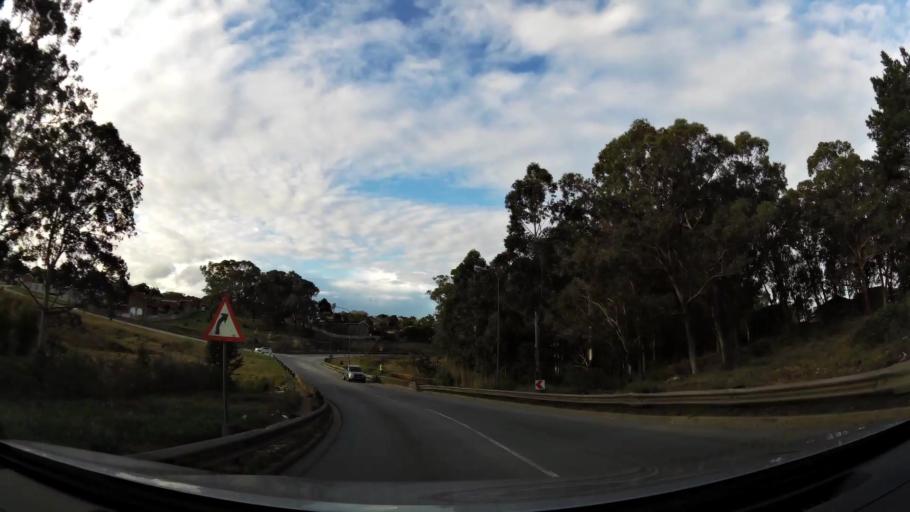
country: ZA
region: Eastern Cape
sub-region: Nelson Mandela Bay Metropolitan Municipality
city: Port Elizabeth
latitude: -33.9540
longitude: 25.5072
